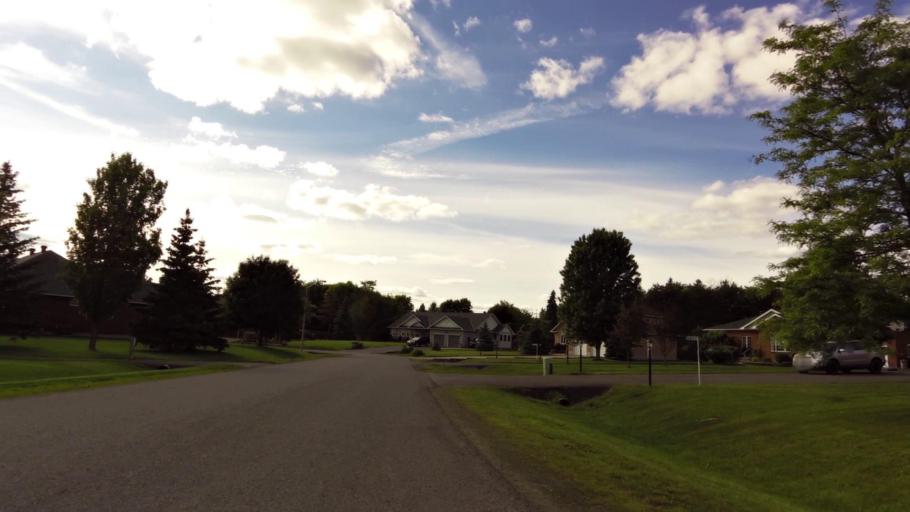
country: CA
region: Ontario
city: Ottawa
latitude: 45.2729
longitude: -75.5778
